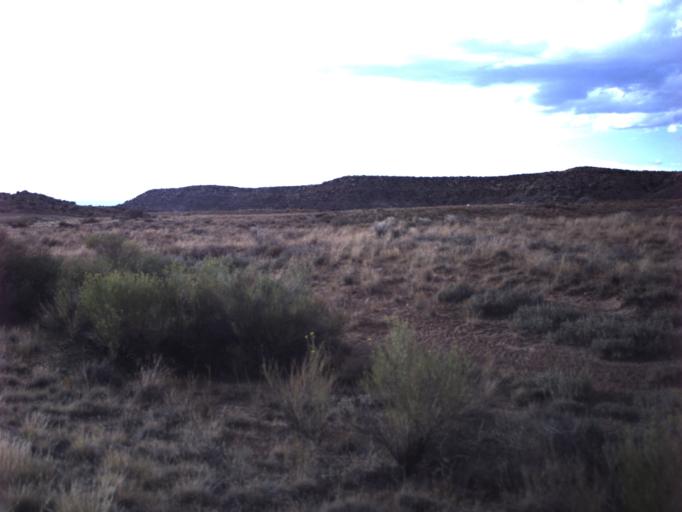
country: US
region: Utah
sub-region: San Juan County
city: Blanding
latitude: 37.4228
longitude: -109.4702
